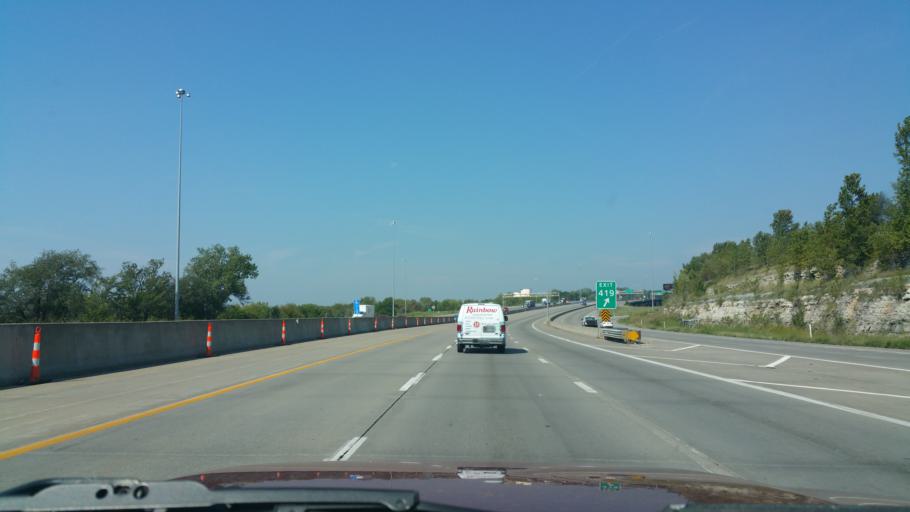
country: US
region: Kansas
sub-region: Wyandotte County
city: Kansas City
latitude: 39.0986
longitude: -94.6645
